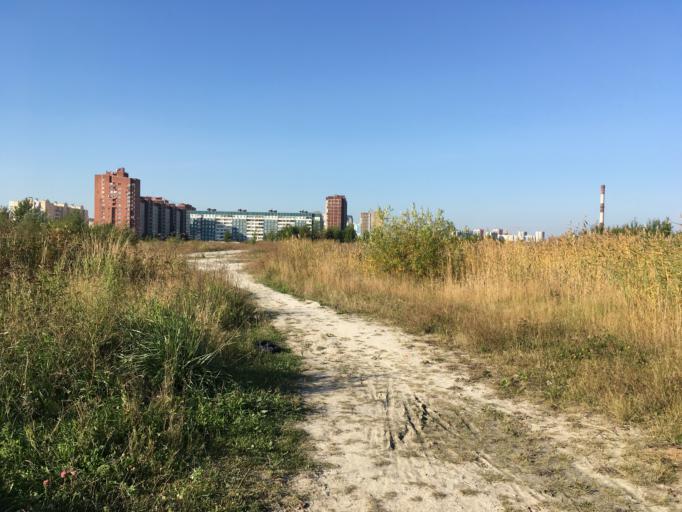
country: RU
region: St.-Petersburg
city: Komendantsky aerodrom
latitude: 60.0178
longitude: 30.2634
